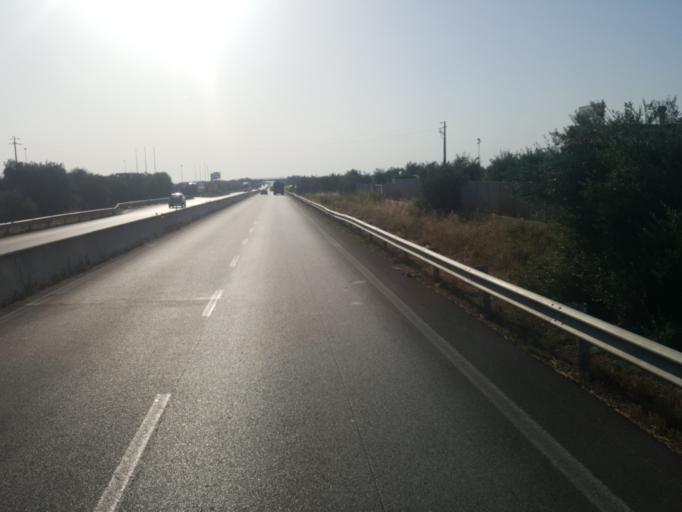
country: IT
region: Apulia
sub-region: Provincia di Barletta - Andria - Trani
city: San Ferdinando di Puglia
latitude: 41.3111
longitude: 16.0817
